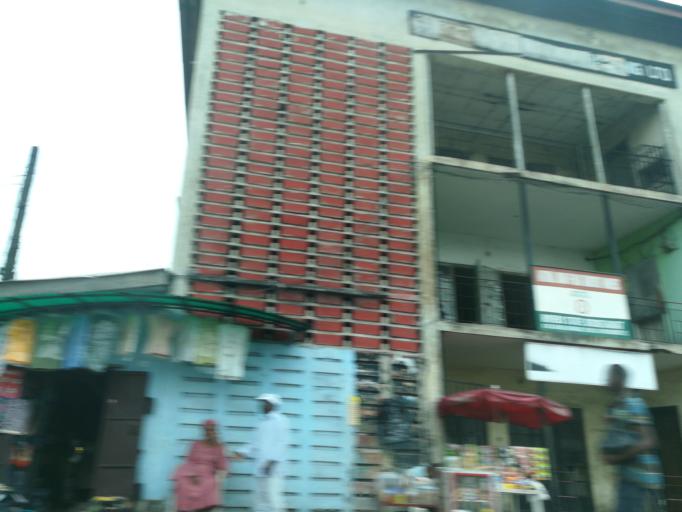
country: NG
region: Rivers
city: Port Harcourt
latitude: 4.8359
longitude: 7.0219
